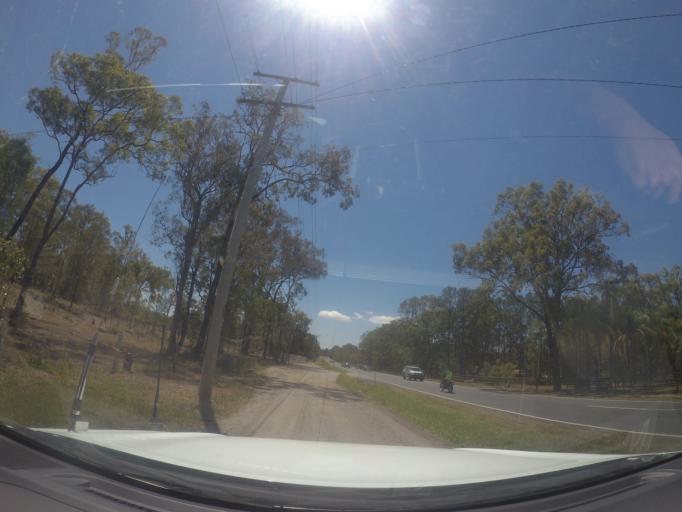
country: AU
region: Queensland
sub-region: Logan
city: Logan Reserve
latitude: -27.7393
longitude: 153.1275
